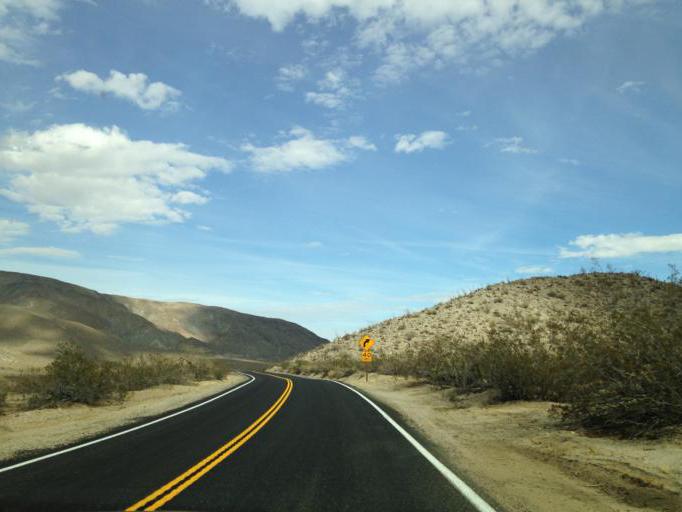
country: US
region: California
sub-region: San Diego County
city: Borrego Springs
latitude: 33.1312
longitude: -116.4040
